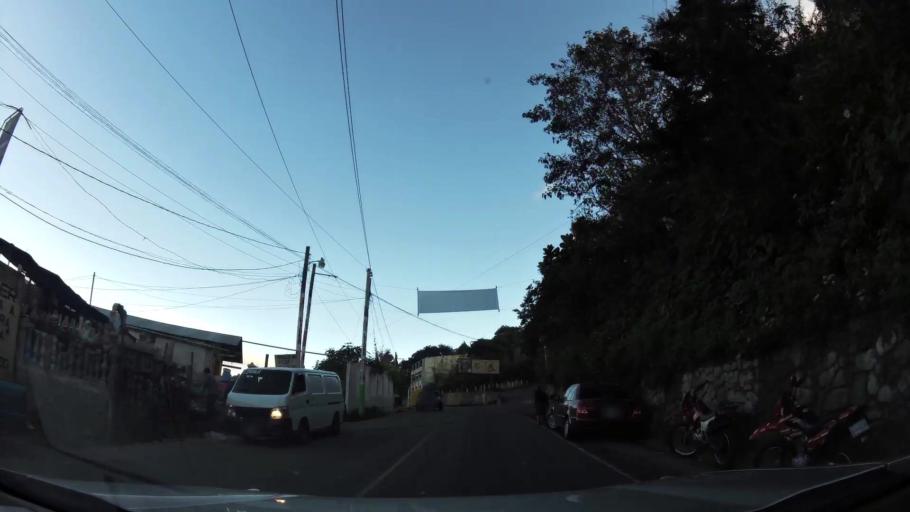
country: GT
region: Quiche
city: Chichicastenango
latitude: 14.9365
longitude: -91.1104
